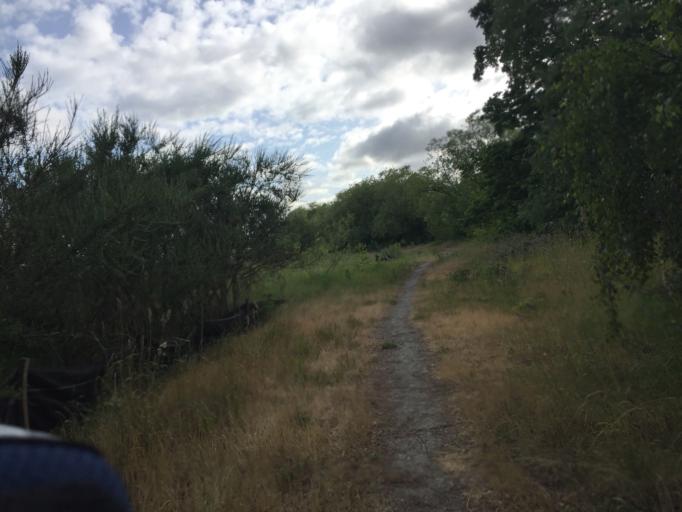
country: CA
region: British Columbia
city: Richmond
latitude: 49.1816
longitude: -123.1463
